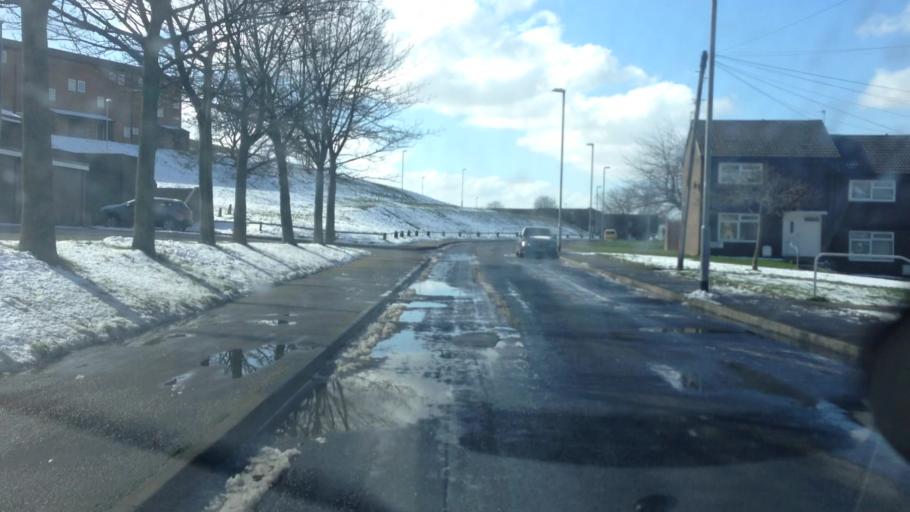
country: GB
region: England
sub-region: City and Borough of Leeds
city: Chapel Allerton
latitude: 53.8272
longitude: -1.5544
